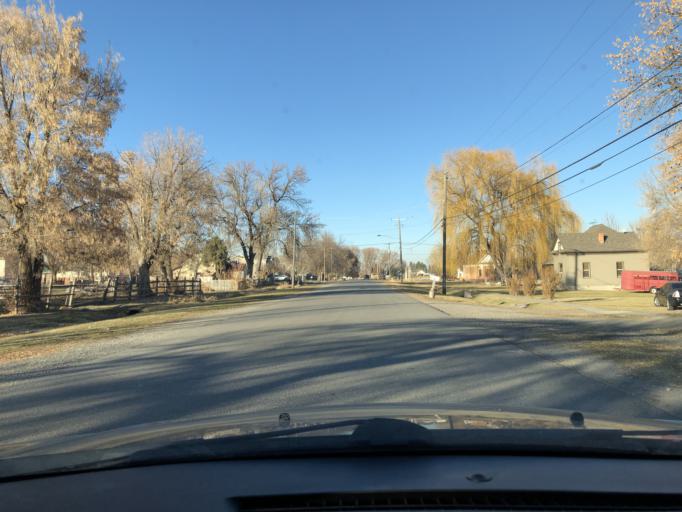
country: US
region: Utah
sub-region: Cache County
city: Wellsville
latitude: 41.6419
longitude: -111.9314
